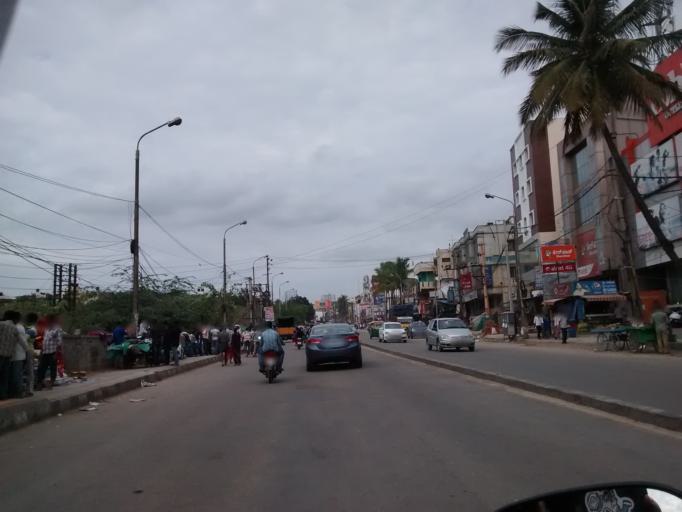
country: IN
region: Karnataka
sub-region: Bangalore Urban
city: Bangalore
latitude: 12.9565
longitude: 77.6952
